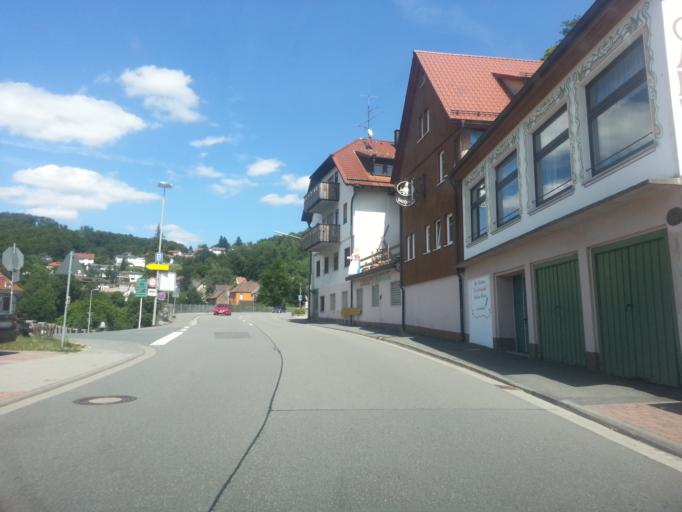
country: DE
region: Hesse
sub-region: Regierungsbezirk Darmstadt
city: Lindenfels
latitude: 49.6862
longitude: 8.7799
